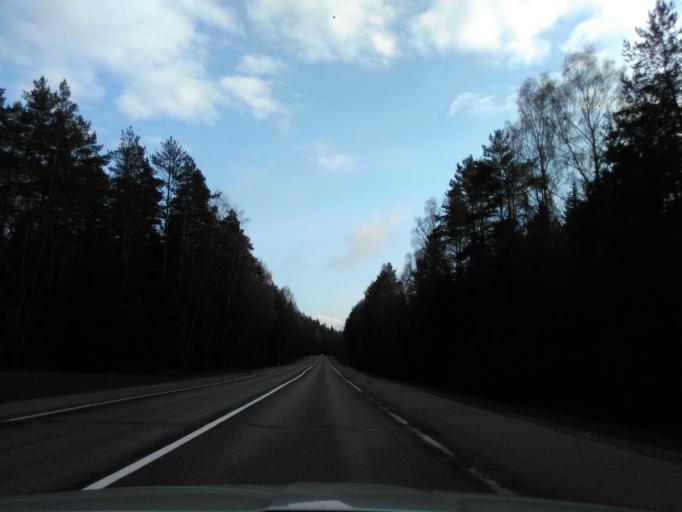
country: BY
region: Minsk
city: Lahoysk
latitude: 54.2554
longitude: 27.8527
